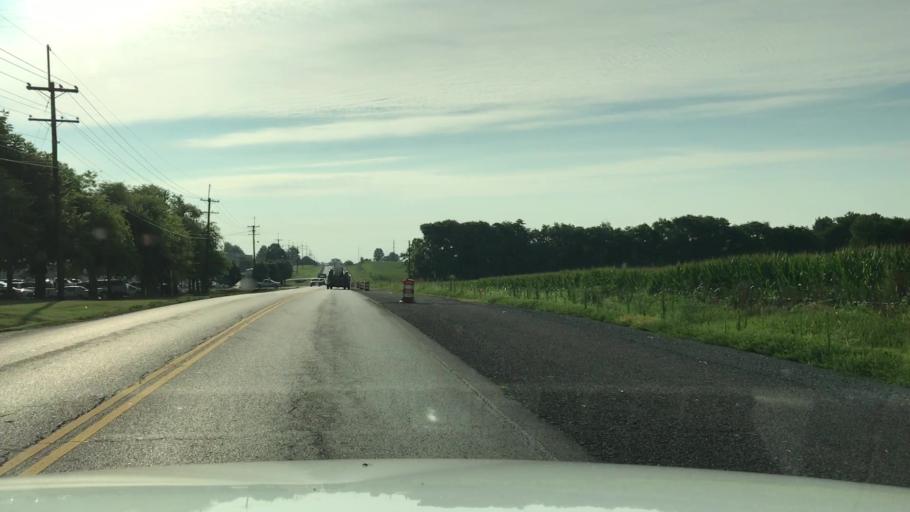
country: US
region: Tennessee
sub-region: Sumner County
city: Gallatin
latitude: 36.3758
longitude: -86.4303
